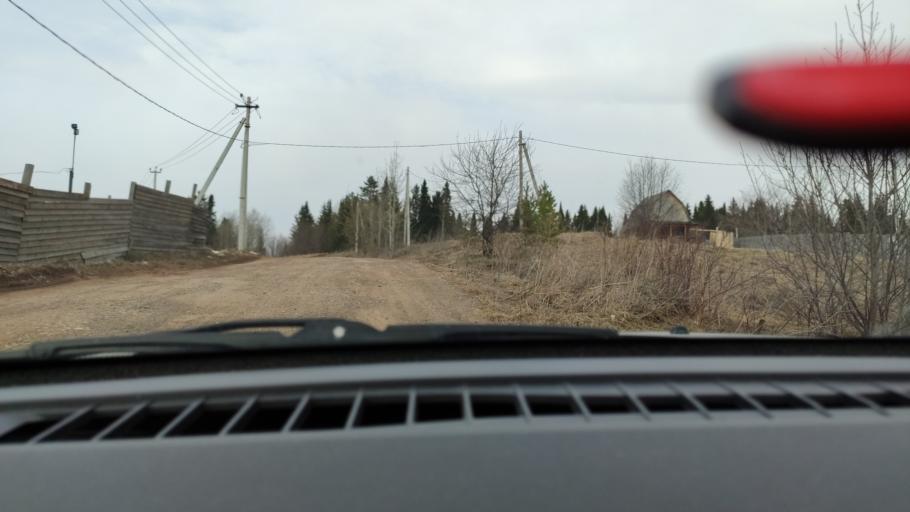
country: RU
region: Perm
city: Kultayevo
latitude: 57.8977
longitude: 56.0129
